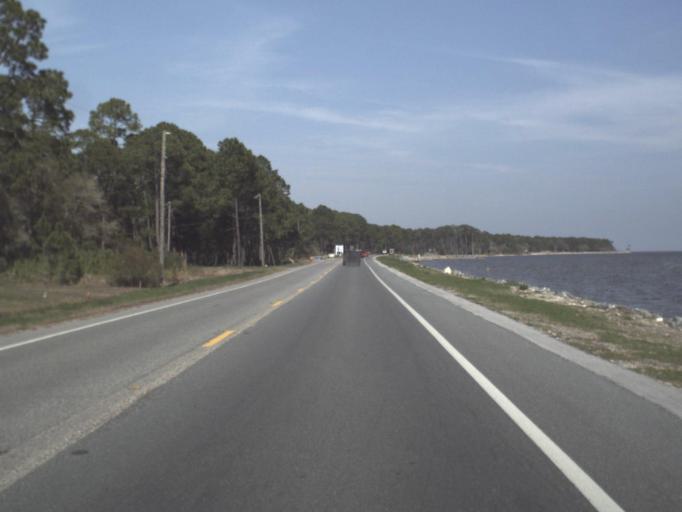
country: US
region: Florida
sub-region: Franklin County
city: Eastpoint
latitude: 29.7539
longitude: -84.8417
